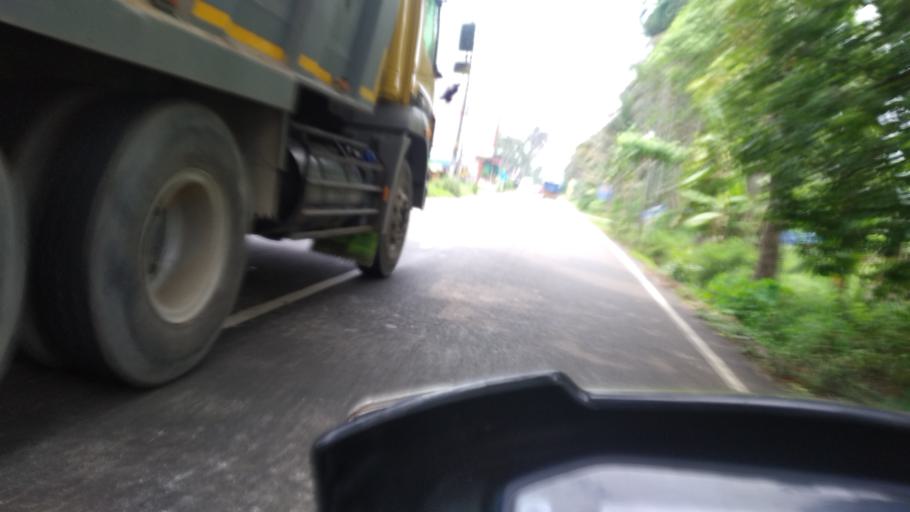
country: IN
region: Kerala
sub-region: Ernakulam
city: Aluva
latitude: 10.1562
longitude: 76.3089
